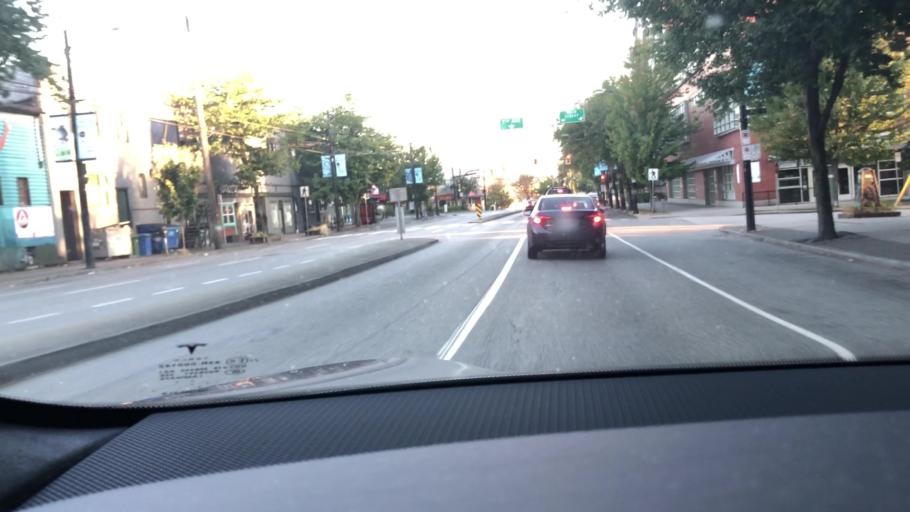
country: CA
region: British Columbia
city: Vancouver
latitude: 49.2633
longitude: -123.0998
